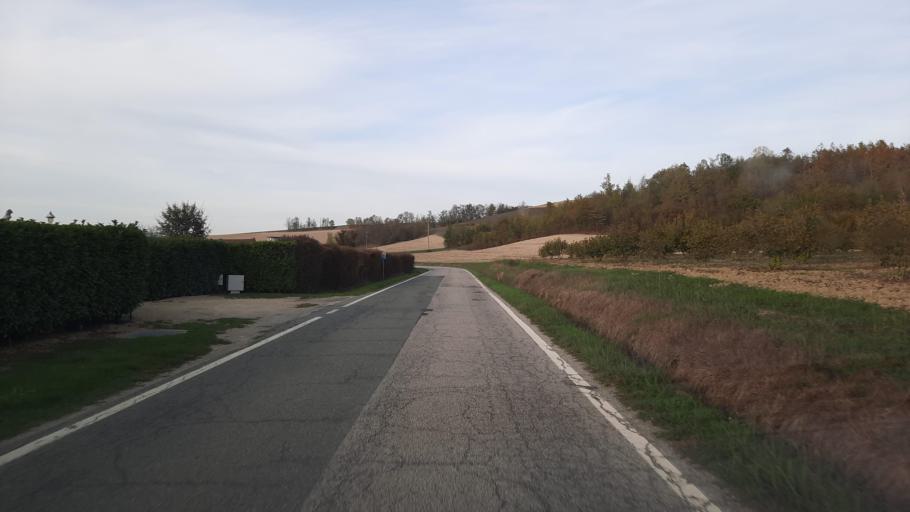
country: IT
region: Piedmont
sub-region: Provincia di Asti
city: Castell'Alfero
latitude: 44.9960
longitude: 8.2232
